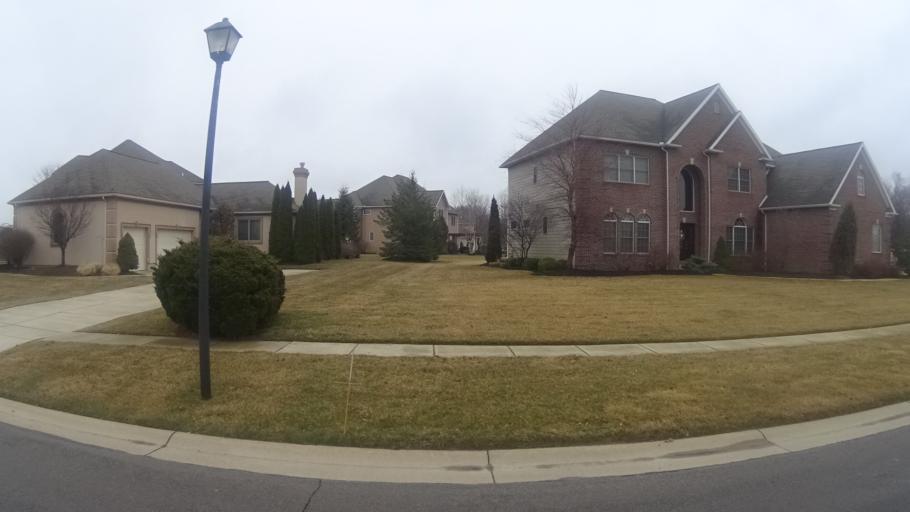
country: US
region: Ohio
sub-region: Erie County
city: Sandusky
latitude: 41.4189
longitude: -82.6531
